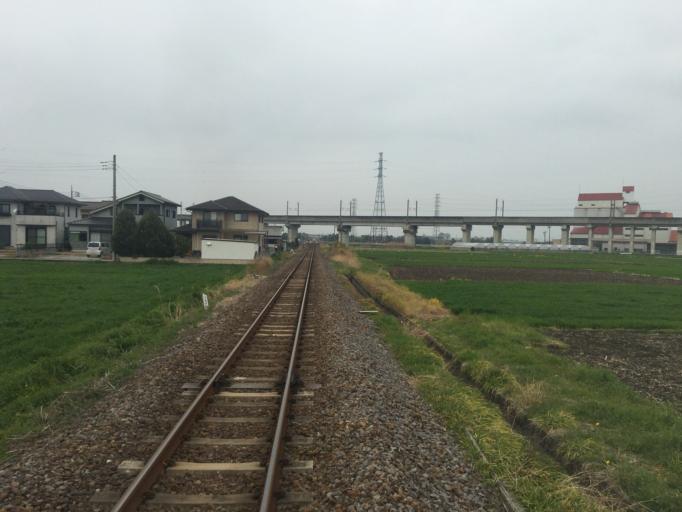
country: JP
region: Gunma
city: Fujioka
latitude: 36.2659
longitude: 139.0836
